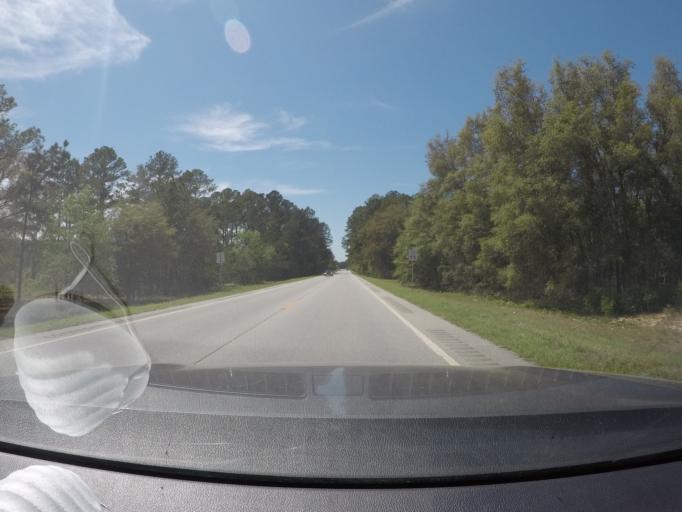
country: US
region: Georgia
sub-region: Evans County
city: Claxton
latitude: 32.1475
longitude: -81.7721
